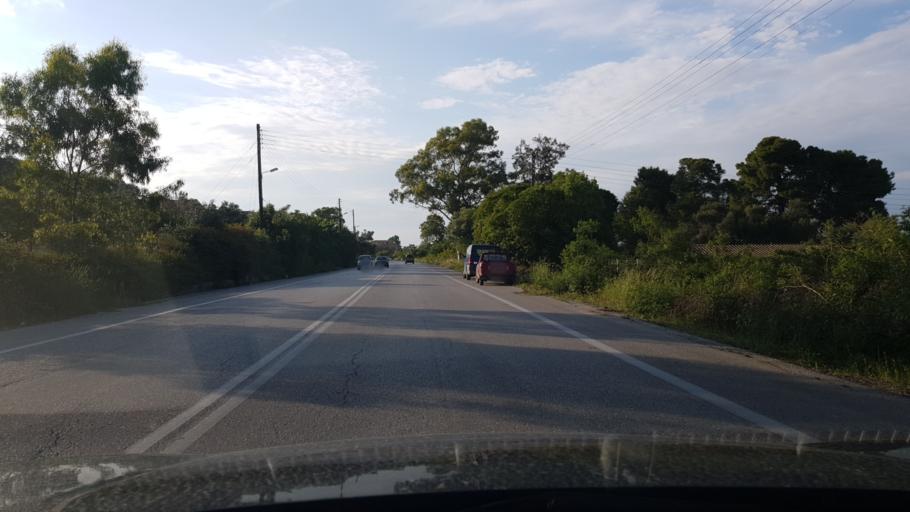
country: GR
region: Ionian Islands
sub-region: Lefkada
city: Lefkada
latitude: 38.8123
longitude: 20.7149
